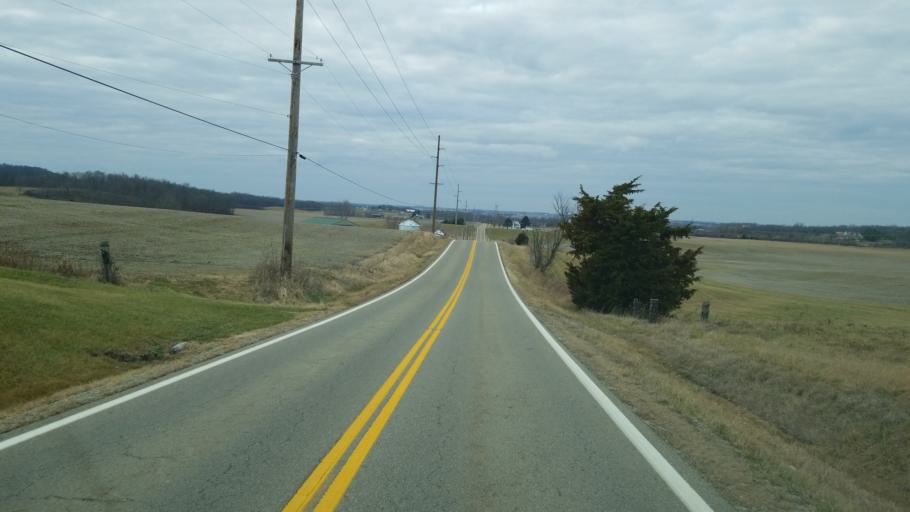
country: US
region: Ohio
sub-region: Ross County
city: Frankfort
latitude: 39.3547
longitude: -83.2588
